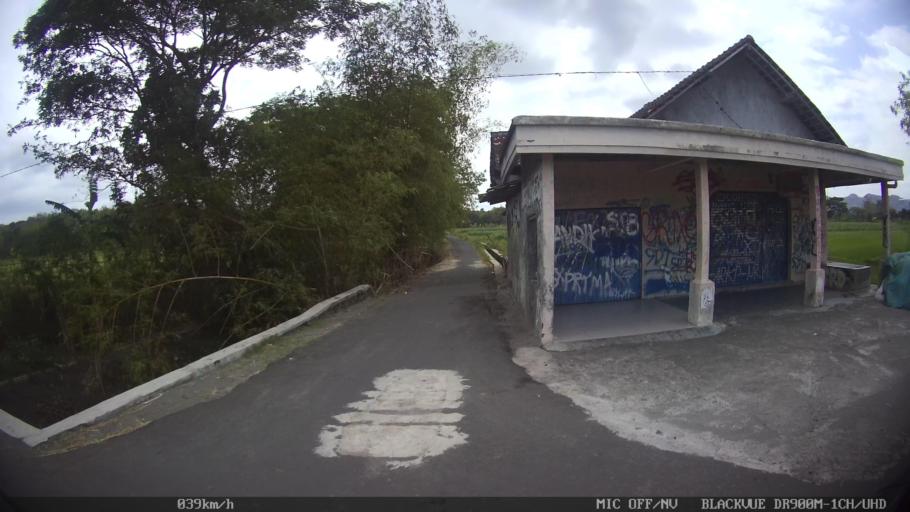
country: ID
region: Daerah Istimewa Yogyakarta
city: Depok
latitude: -7.8138
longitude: 110.4737
